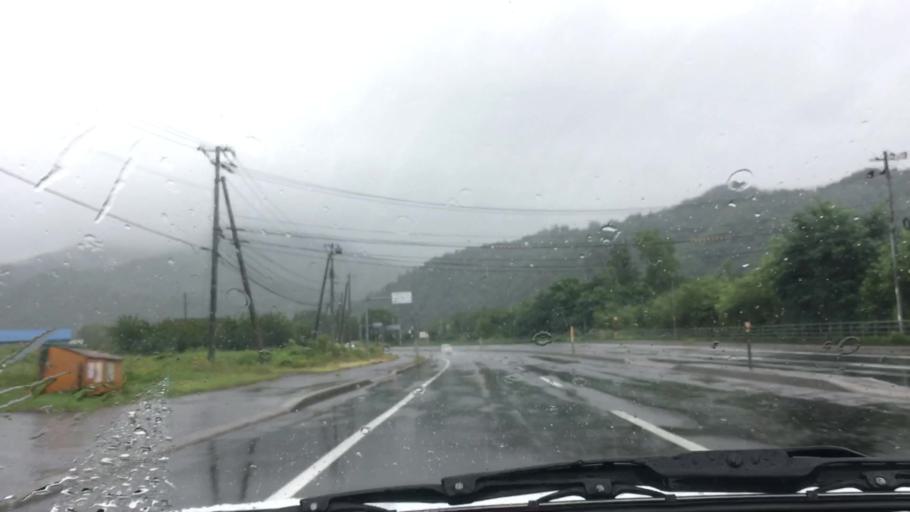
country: JP
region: Hokkaido
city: Sapporo
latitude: 42.9633
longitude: 141.2216
